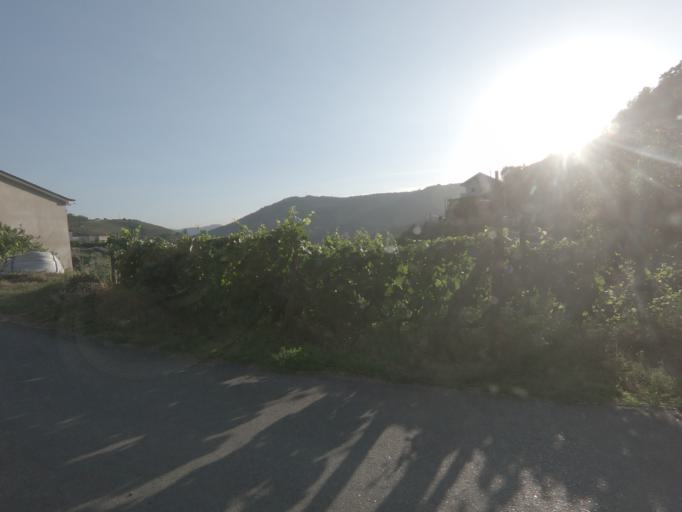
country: PT
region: Vila Real
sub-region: Sabrosa
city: Vilela
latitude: 41.1877
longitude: -7.6325
